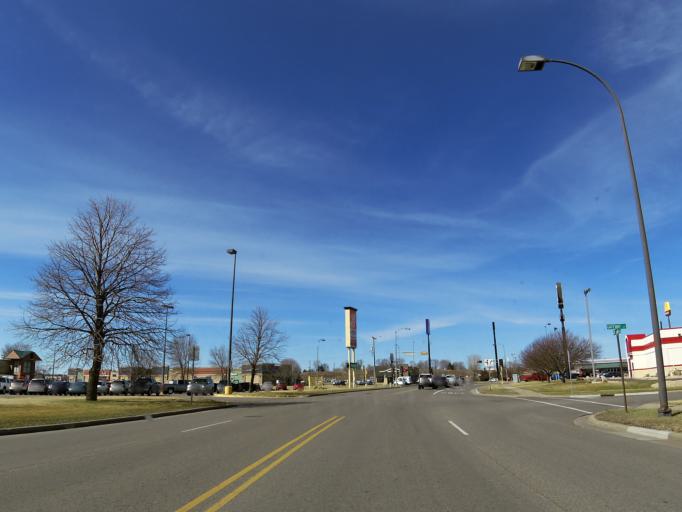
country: US
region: Wisconsin
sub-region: Saint Croix County
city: Hudson
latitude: 44.9598
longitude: -92.7235
